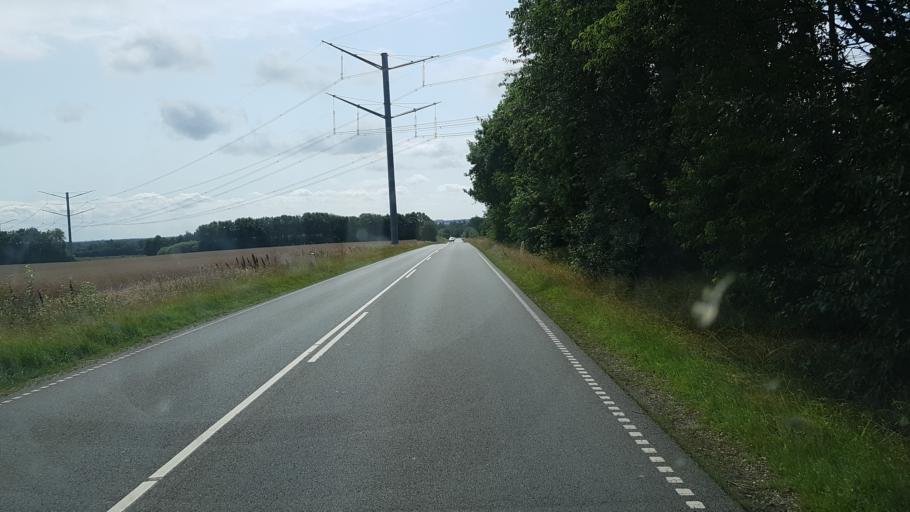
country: DK
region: South Denmark
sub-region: Vejen Kommune
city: Vejen
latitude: 55.5799
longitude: 9.1579
